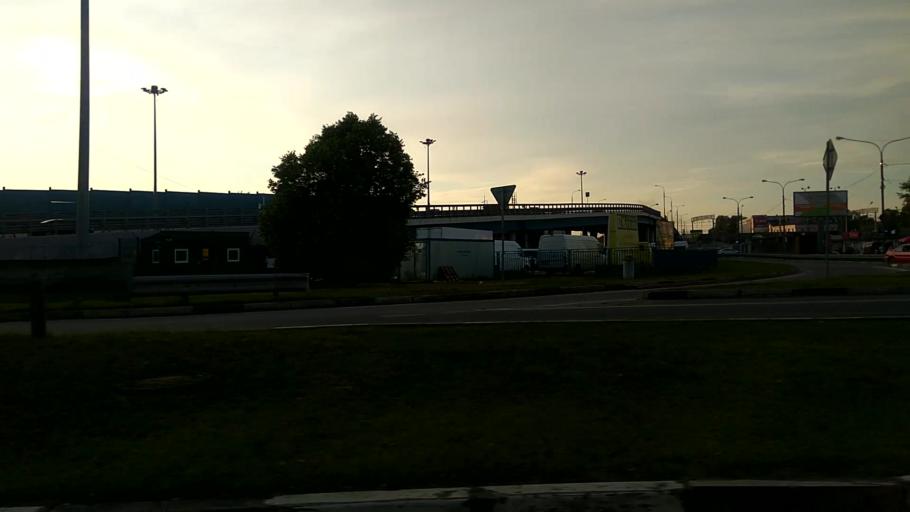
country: RU
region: Moskovskaya
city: Yubileyny
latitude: 55.9241
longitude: 37.8575
